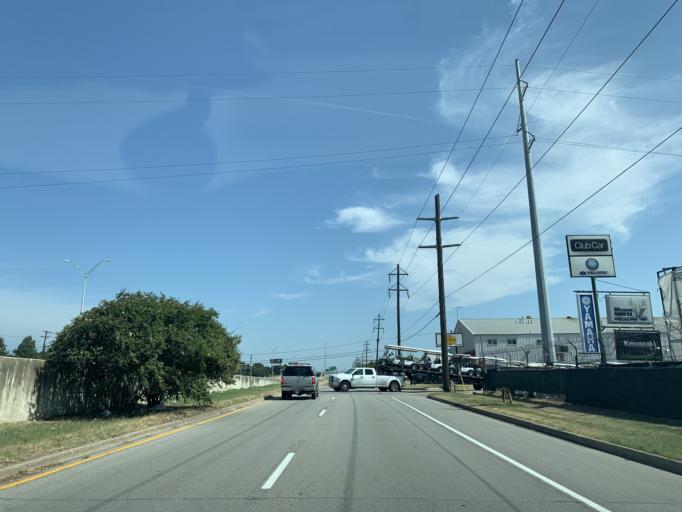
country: US
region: Texas
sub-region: Tarrant County
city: Fort Worth
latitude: 32.6889
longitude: -97.3203
